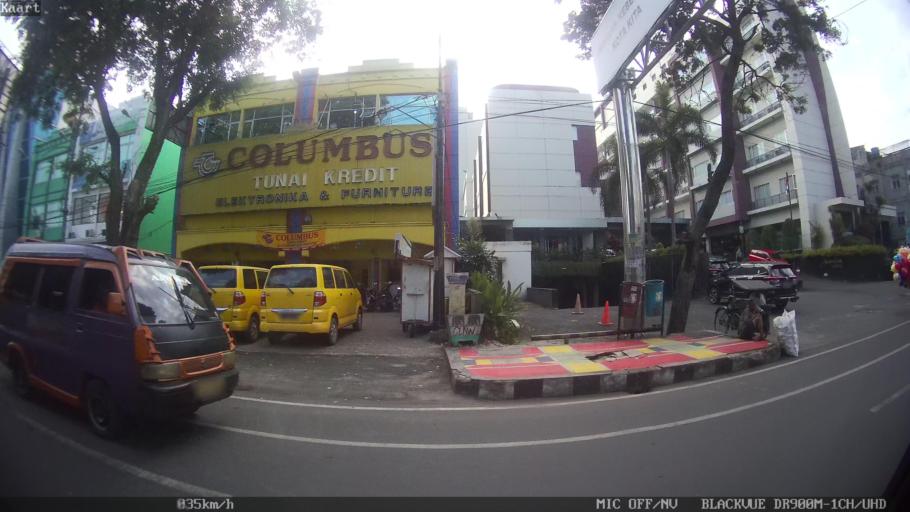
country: ID
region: Lampung
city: Bandarlampung
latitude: -5.4155
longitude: 105.2582
